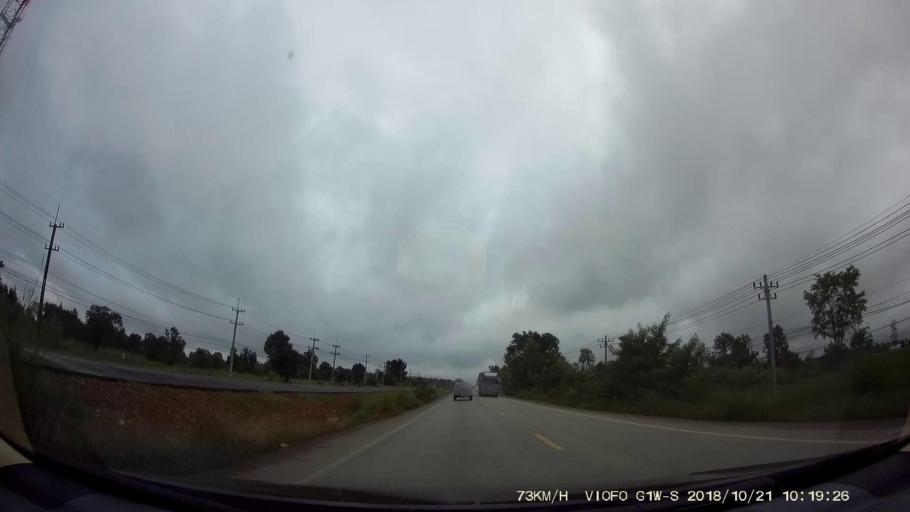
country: TH
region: Chaiyaphum
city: Phu Khiao
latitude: 16.3146
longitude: 102.1986
